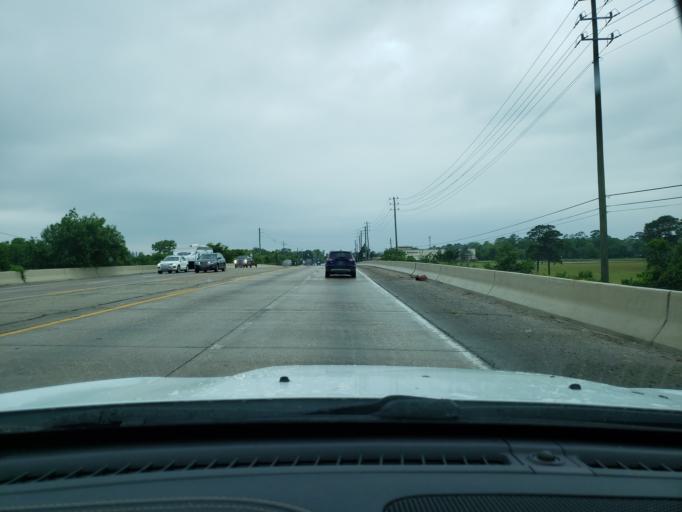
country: US
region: Texas
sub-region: Harris County
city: Baytown
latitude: 29.7709
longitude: -94.9162
